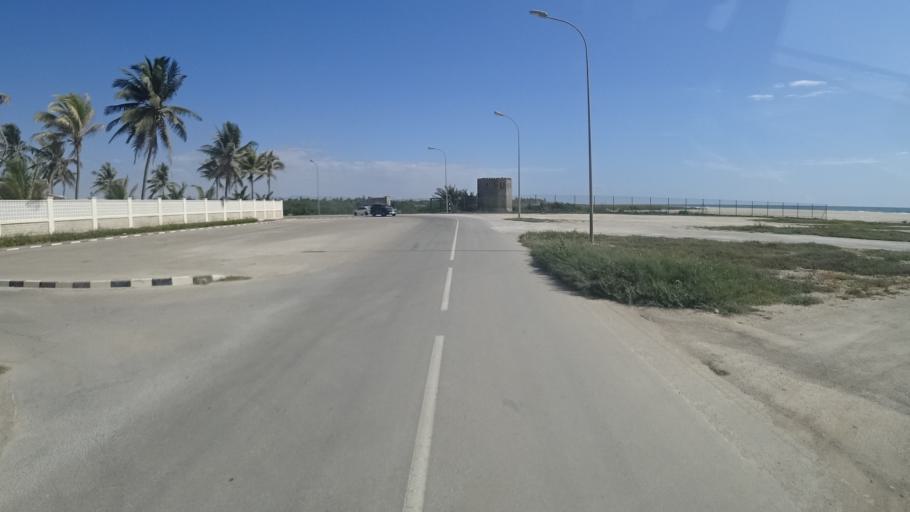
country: OM
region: Zufar
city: Salalah
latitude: 16.9951
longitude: 54.0649
